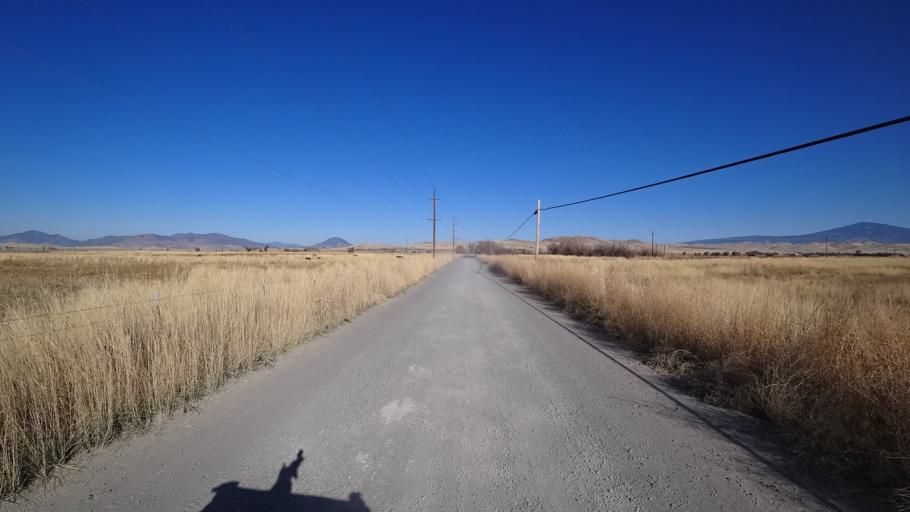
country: US
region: California
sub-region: Siskiyou County
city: Montague
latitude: 41.7099
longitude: -122.4377
